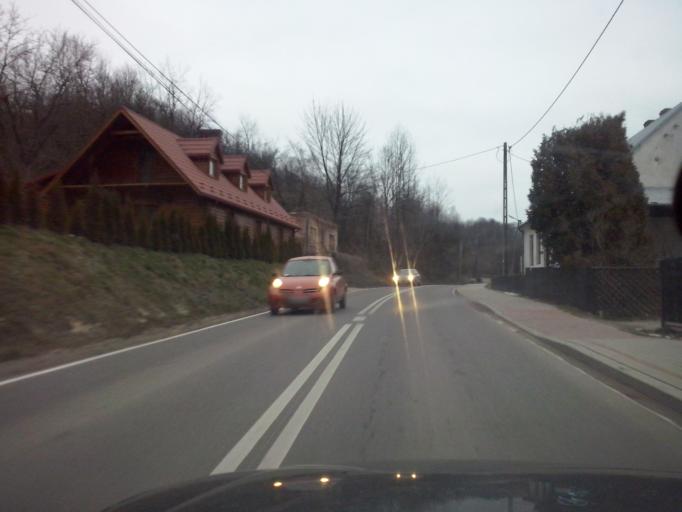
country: PL
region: Subcarpathian Voivodeship
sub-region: Powiat nizanski
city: Krzeszow
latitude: 50.4062
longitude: 22.3413
